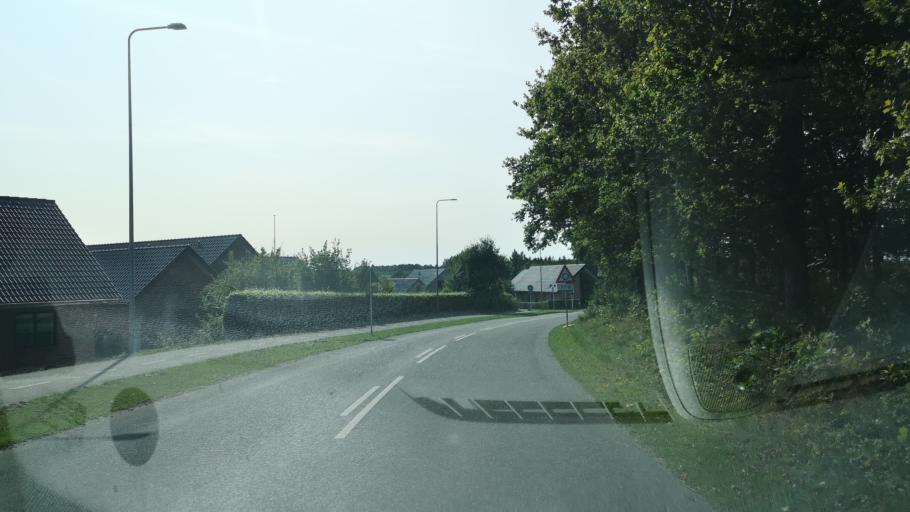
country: DK
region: Central Jutland
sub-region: Ringkobing-Skjern Kommune
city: Videbaek
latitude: 56.0800
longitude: 8.6180
